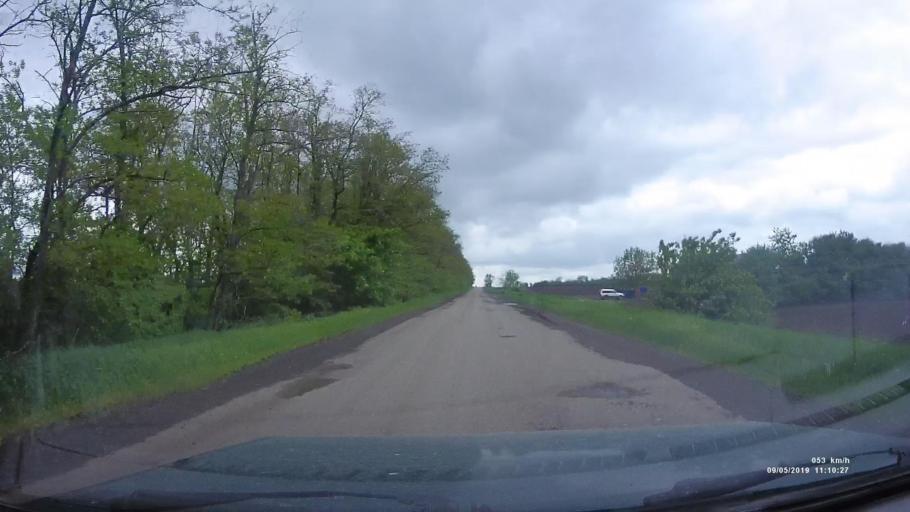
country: RU
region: Krasnodarskiy
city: Kanelovskaya
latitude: 46.7749
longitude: 39.2119
